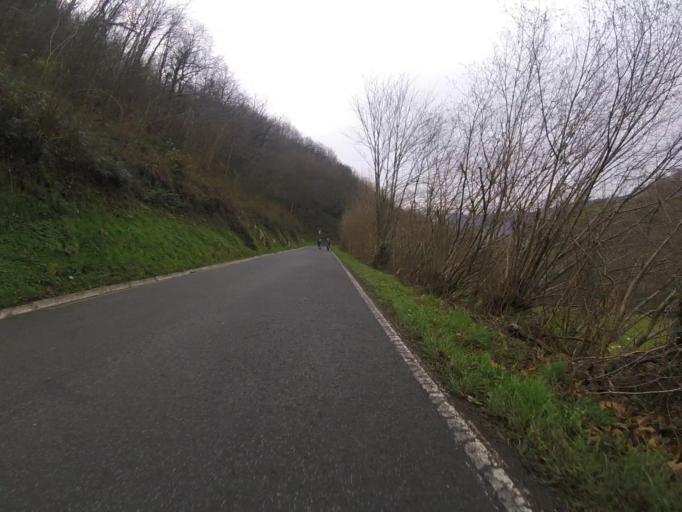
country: ES
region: Navarre
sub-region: Provincia de Navarra
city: Arantza
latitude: 43.2059
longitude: -1.7107
